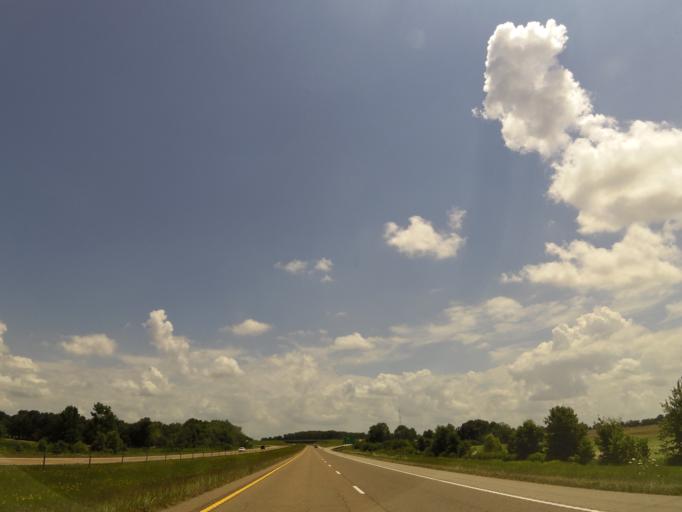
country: US
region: Tennessee
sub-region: Crockett County
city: Alamo
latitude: 35.8055
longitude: -89.1604
